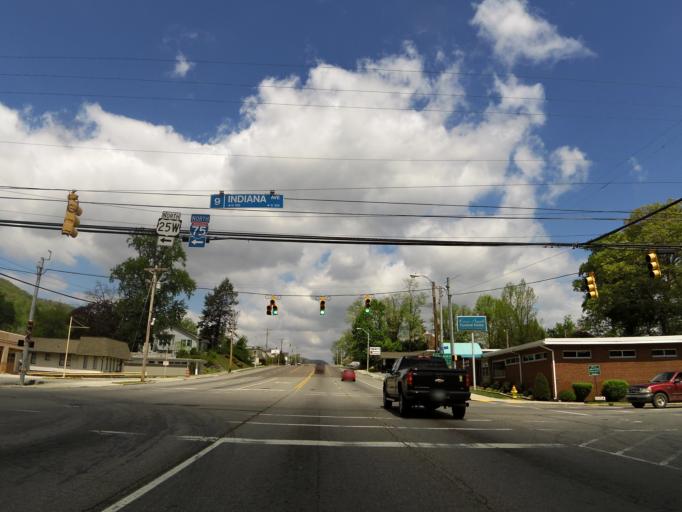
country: US
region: Tennessee
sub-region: Campbell County
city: LaFollette
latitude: 36.3825
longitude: -84.1203
